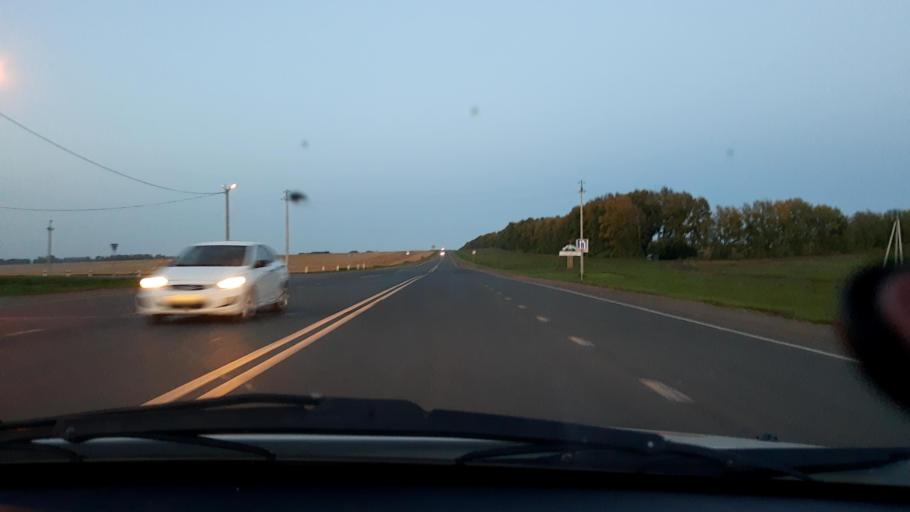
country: RU
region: Bashkortostan
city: Karmaskaly
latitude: 54.3888
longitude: 56.2381
